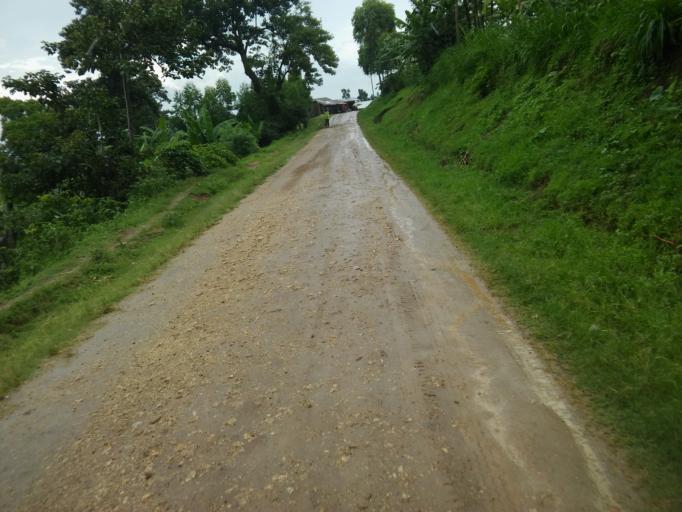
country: UG
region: Eastern Region
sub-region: Mbale District
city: Mbale
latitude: 1.0154
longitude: 34.2260
